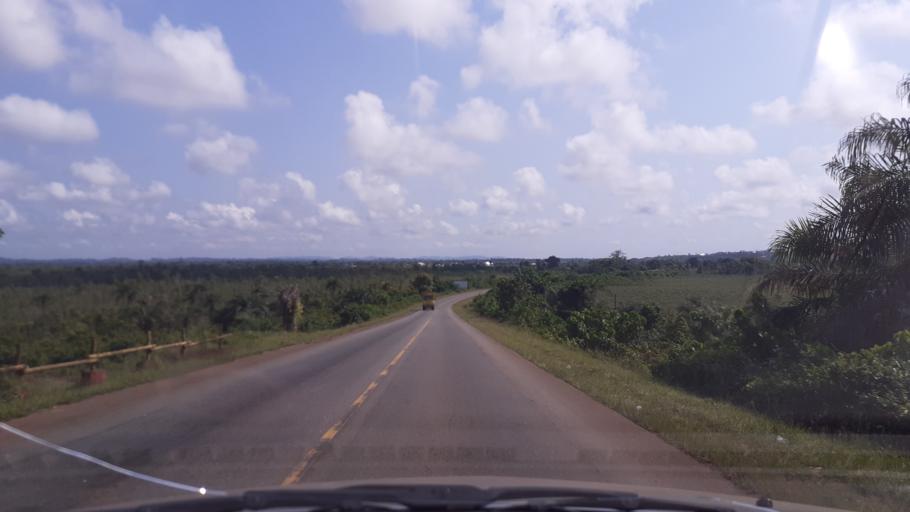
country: LR
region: Montserrado
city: Bensonville City
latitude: 6.2276
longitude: -10.5312
